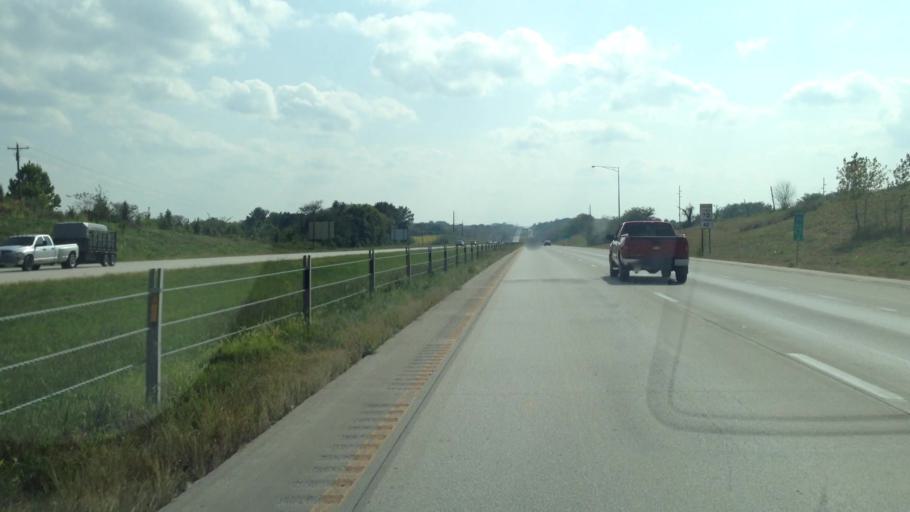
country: US
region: Missouri
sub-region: Clay County
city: Kearney
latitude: 39.3609
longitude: -94.3763
